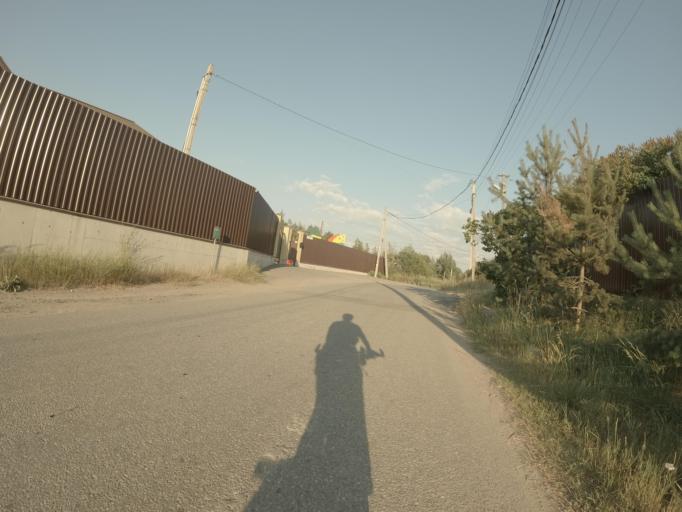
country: RU
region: Leningrad
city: Koltushi
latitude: 59.8954
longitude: 30.6876
